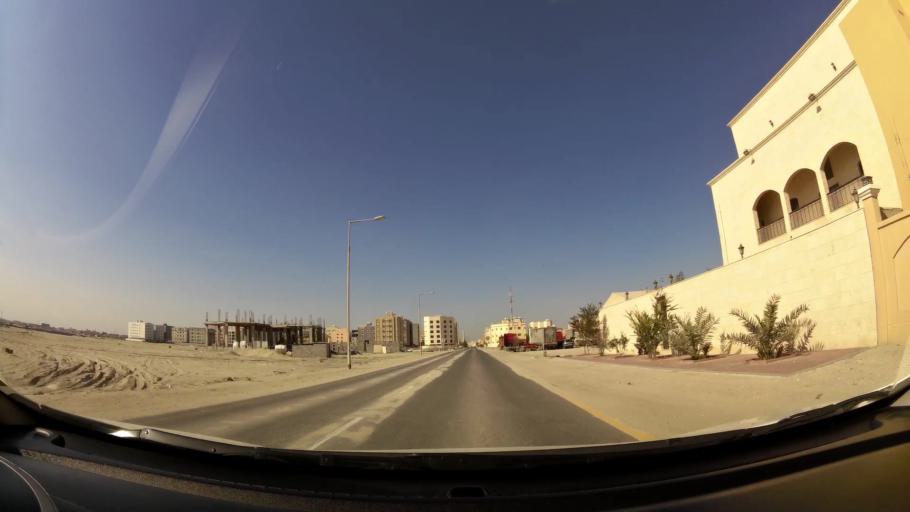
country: BH
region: Muharraq
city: Al Hadd
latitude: 26.2360
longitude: 50.6481
